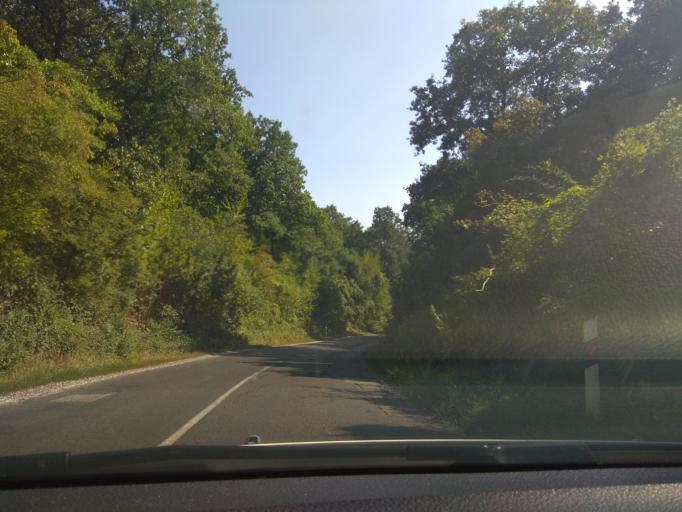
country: HU
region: Borsod-Abauj-Zemplen
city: Harsany
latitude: 48.0222
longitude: 20.7628
